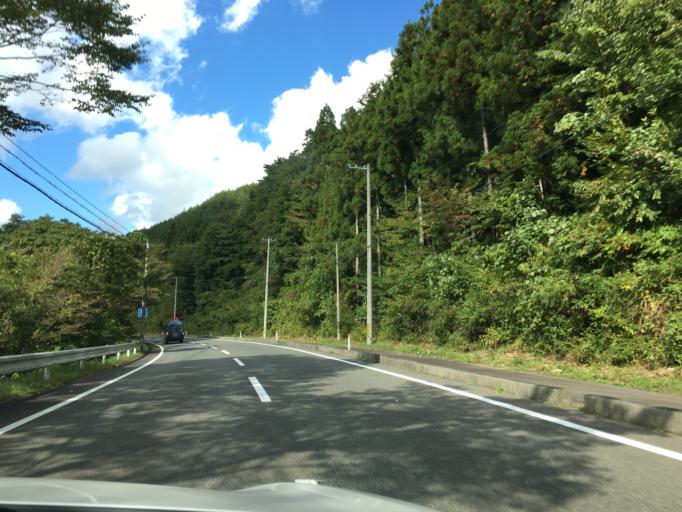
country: JP
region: Fukushima
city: Namie
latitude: 37.5496
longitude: 140.8418
